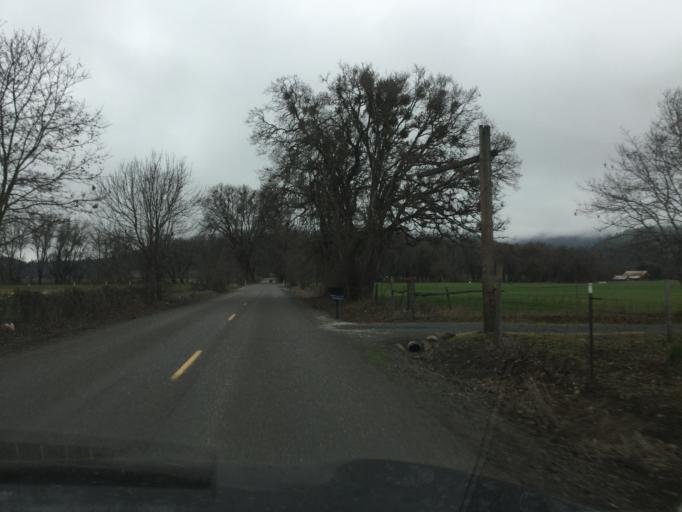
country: US
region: Oregon
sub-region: Jackson County
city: Central Point
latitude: 42.3970
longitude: -122.9686
